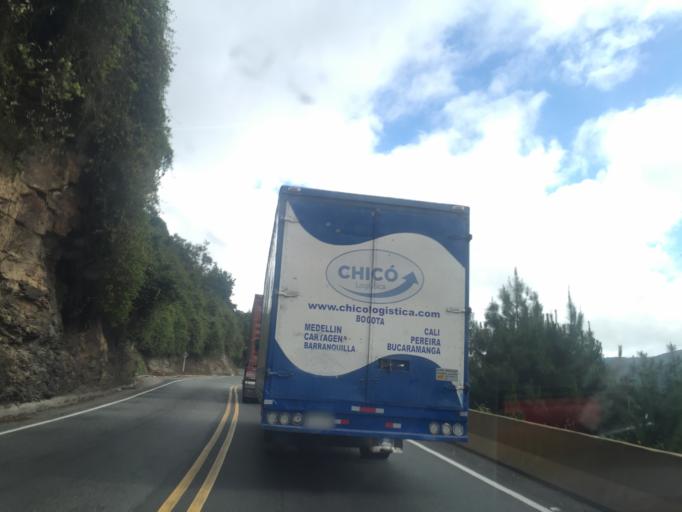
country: CO
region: Tolima
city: Cajamarca
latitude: 4.4583
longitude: -75.5350
